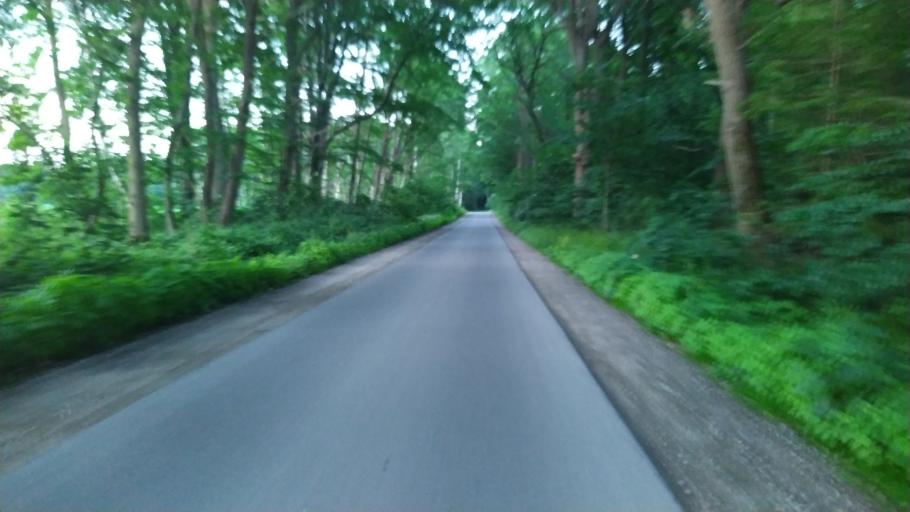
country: DE
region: Lower Saxony
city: Deinstedt
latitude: 53.4911
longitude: 9.2345
